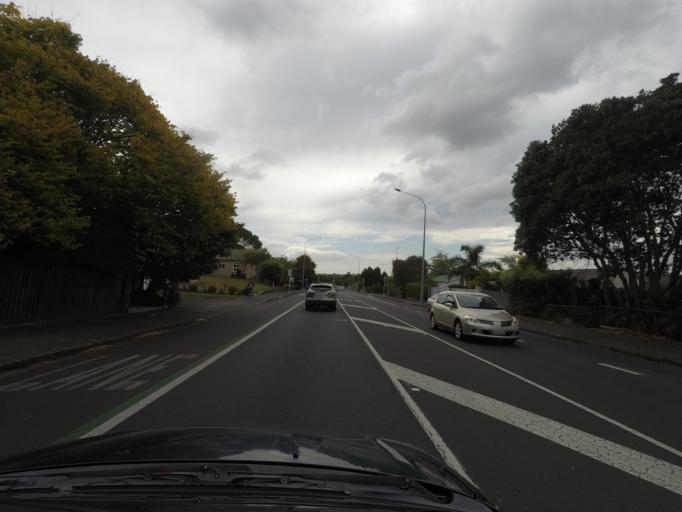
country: NZ
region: Auckland
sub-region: Auckland
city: Auckland
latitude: -36.8951
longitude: 174.7349
